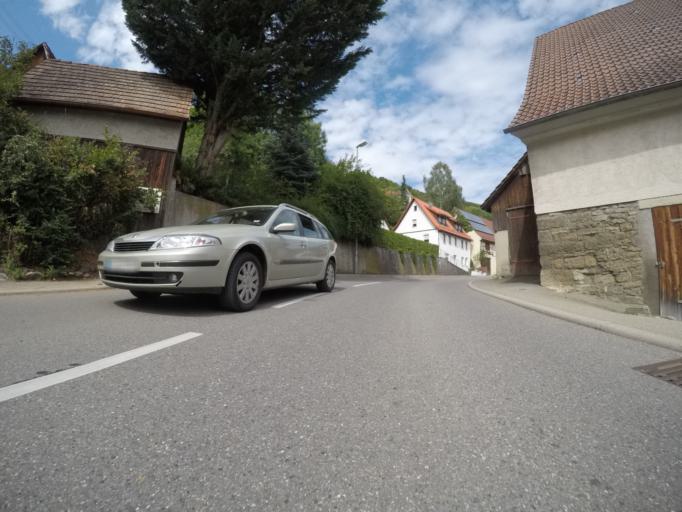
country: DE
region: Baden-Wuerttemberg
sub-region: Tuebingen Region
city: Hirrlingen
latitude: 48.4523
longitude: 8.8572
